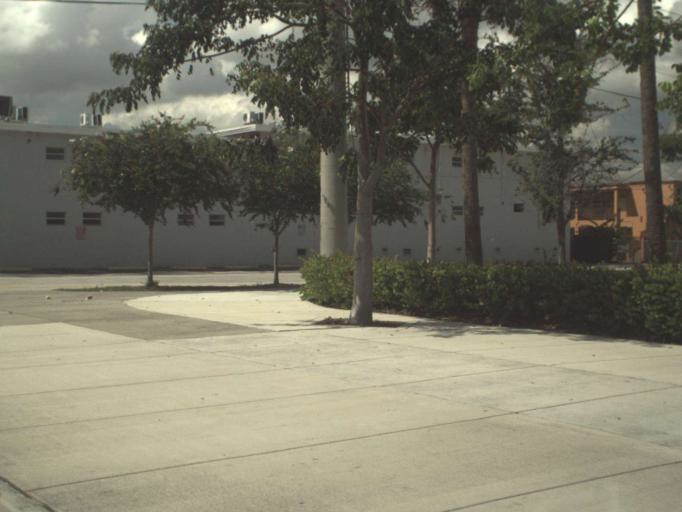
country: US
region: Florida
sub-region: Miami-Dade County
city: El Portal
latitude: 25.8384
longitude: -80.1843
